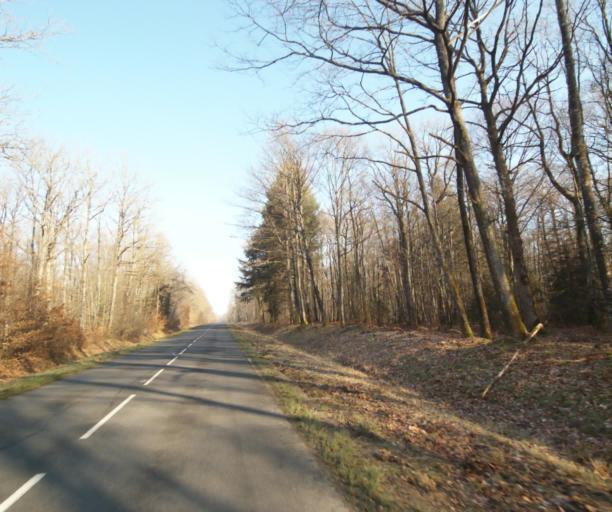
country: FR
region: Champagne-Ardenne
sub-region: Departement de la Haute-Marne
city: Laneuville-a-Remy
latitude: 48.4689
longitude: 4.9176
